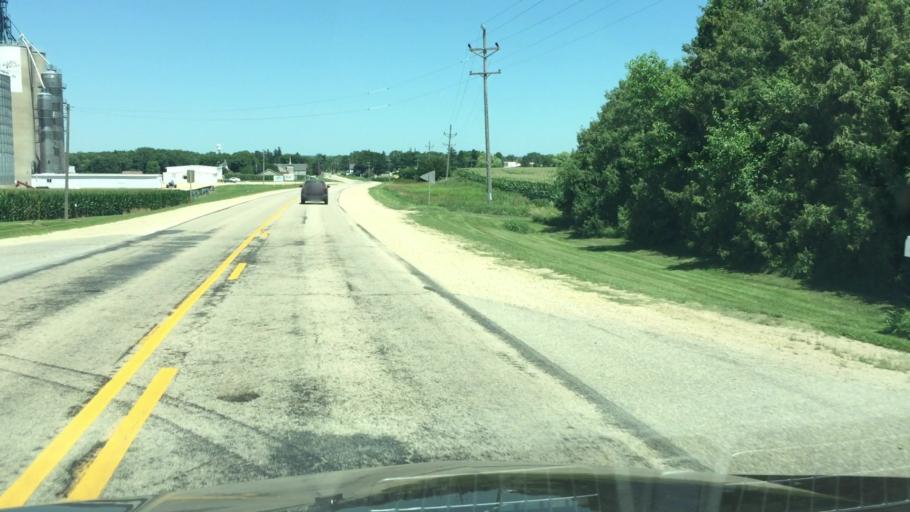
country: US
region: Iowa
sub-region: Cedar County
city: Mechanicsville
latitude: 41.9864
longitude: -91.1418
